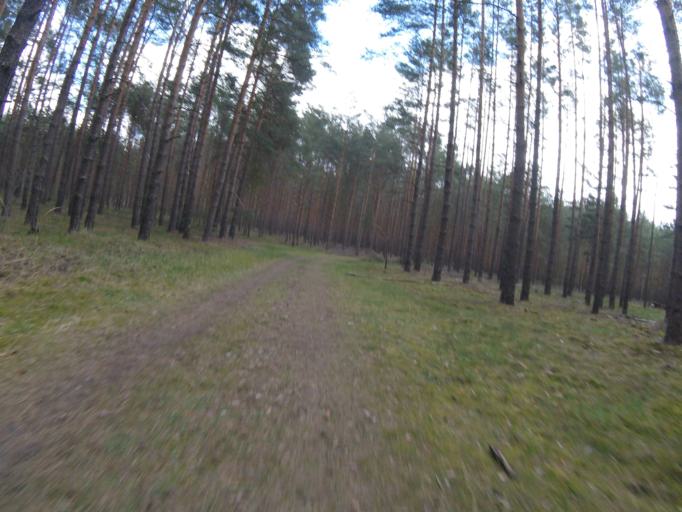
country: DE
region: Brandenburg
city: Bestensee
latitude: 52.2644
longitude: 13.6685
